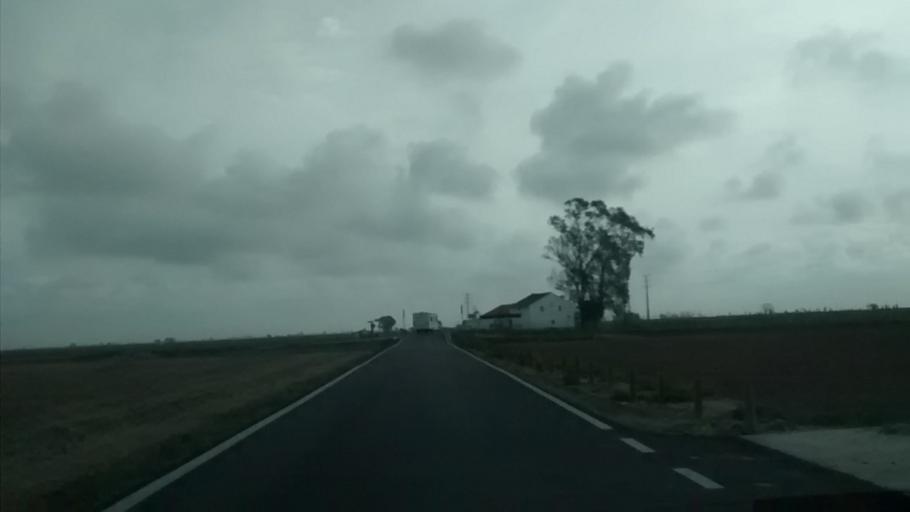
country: ES
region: Catalonia
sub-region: Provincia de Tarragona
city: Deltebre
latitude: 40.6754
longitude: 0.6591
